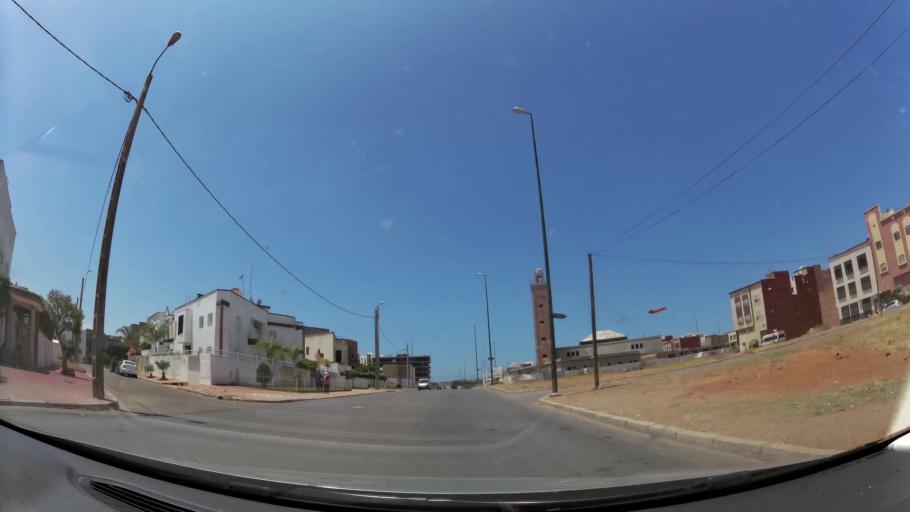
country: MA
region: Gharb-Chrarda-Beni Hssen
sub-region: Kenitra Province
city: Kenitra
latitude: 34.2653
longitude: -6.6218
